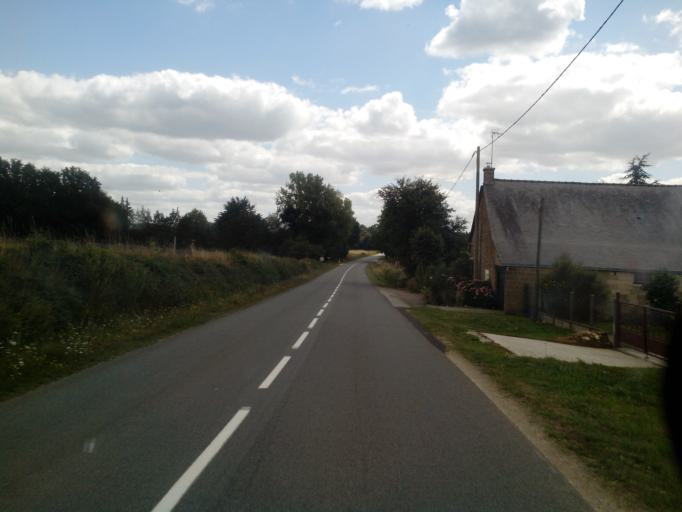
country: FR
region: Brittany
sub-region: Departement des Cotes-d'Armor
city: Plumieux
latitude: 48.0820
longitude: -2.5459
